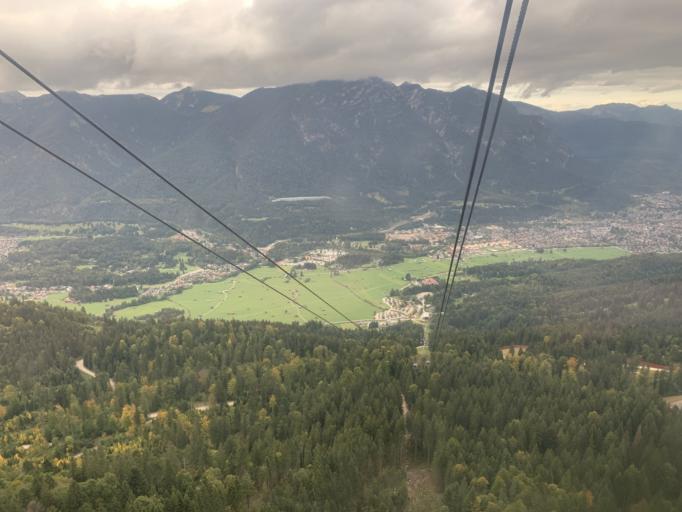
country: DE
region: Bavaria
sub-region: Upper Bavaria
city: Garmisch-Partenkirchen
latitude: 47.4550
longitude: 11.0667
